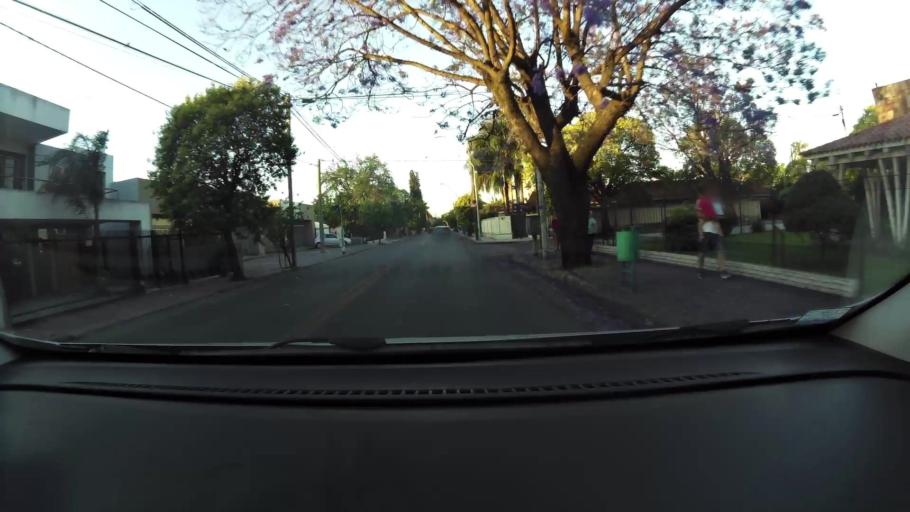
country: AR
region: Cordoba
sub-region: Departamento de Capital
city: Cordoba
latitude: -31.3775
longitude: -64.2231
